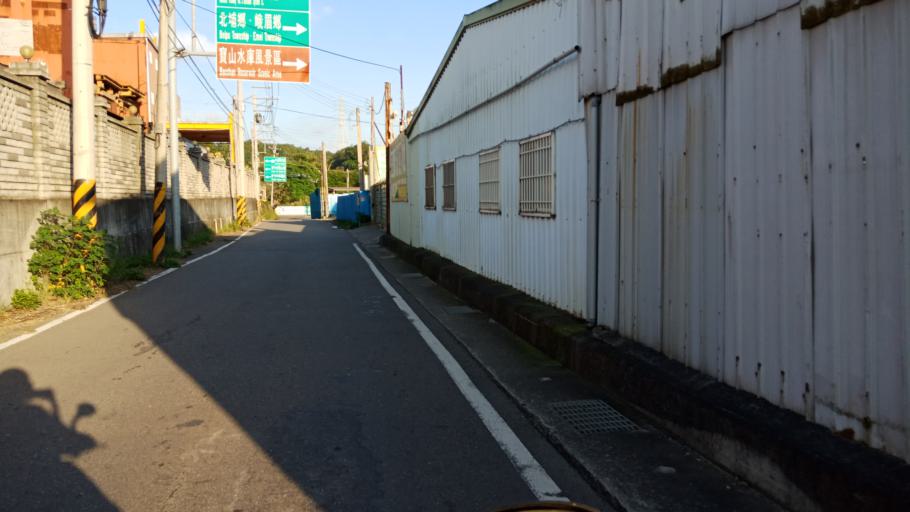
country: TW
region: Taiwan
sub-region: Hsinchu
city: Hsinchu
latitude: 24.7641
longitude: 121.0017
